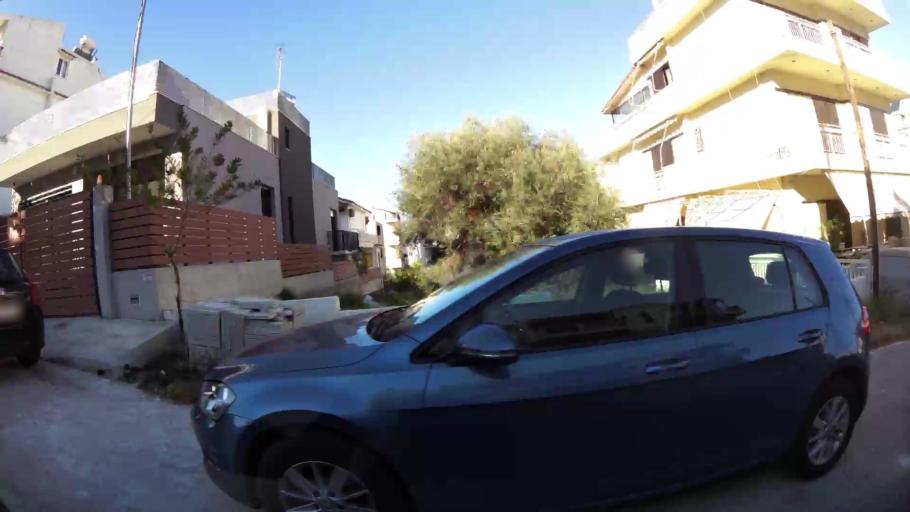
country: GR
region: Attica
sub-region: Nomarchia Athinas
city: Glyfada
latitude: 37.8772
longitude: 23.7714
